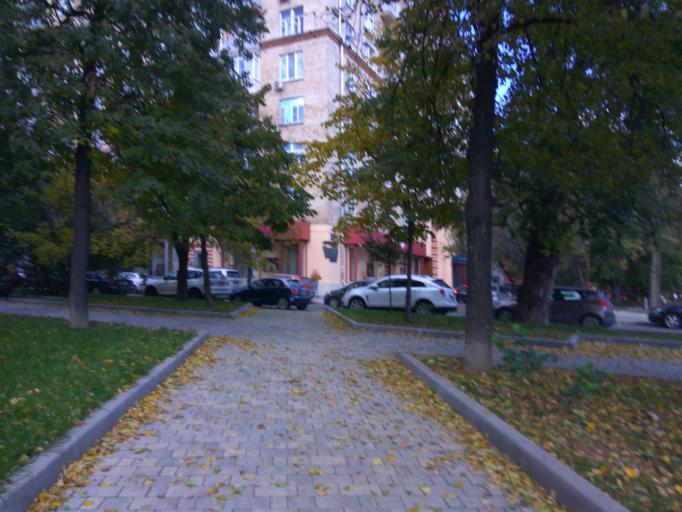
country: RU
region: Moscow
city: Novyye Cheremushki
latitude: 55.7216
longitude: 37.5851
